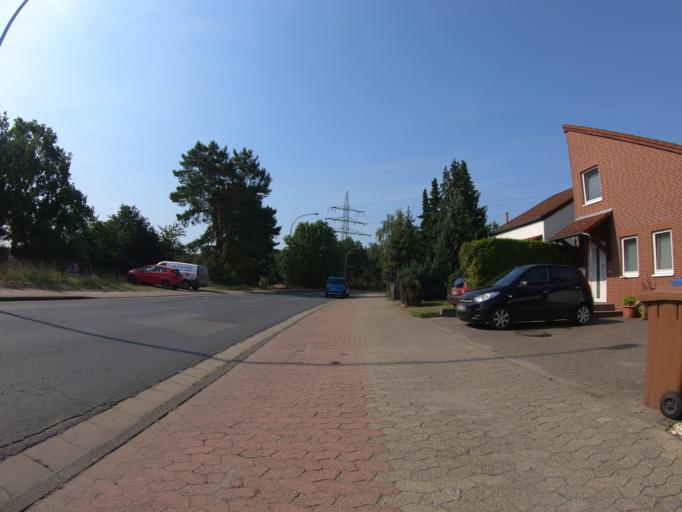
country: DE
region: Lower Saxony
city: Gifhorn
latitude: 52.4734
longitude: 10.5341
